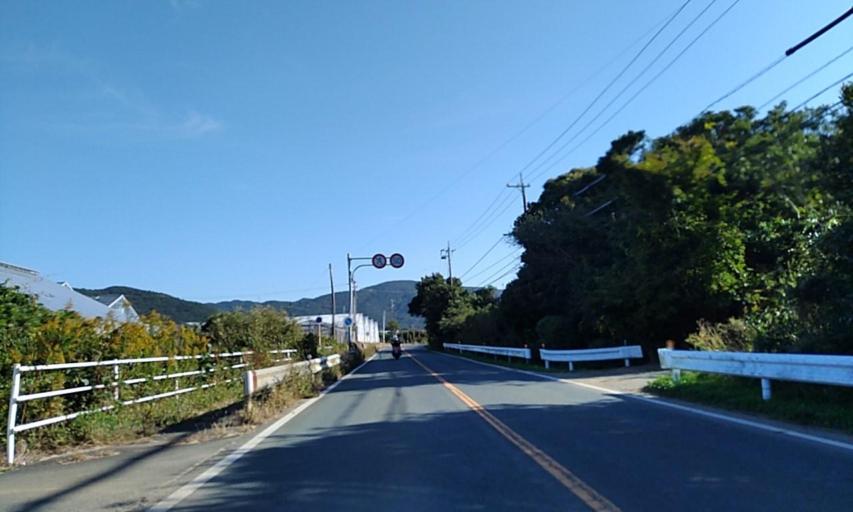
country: JP
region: Aichi
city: Tahara
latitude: 34.5914
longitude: 137.1130
